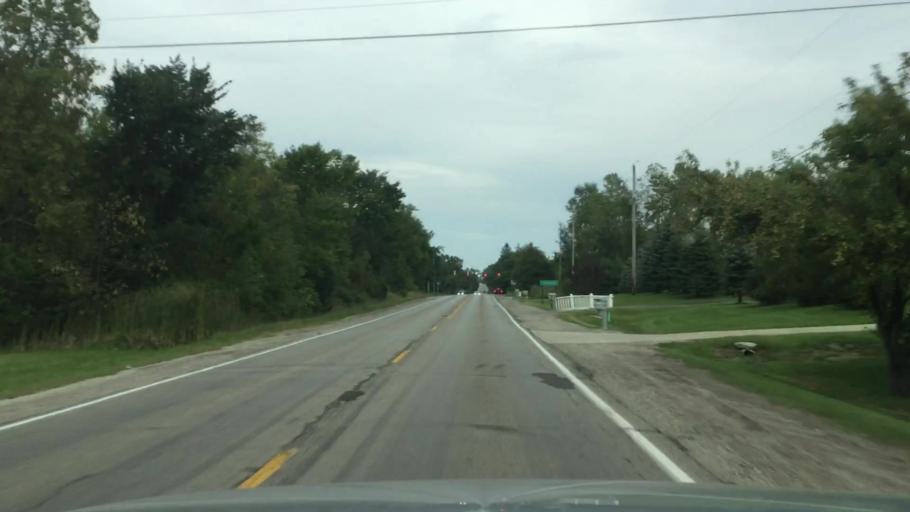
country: US
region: Michigan
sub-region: Genesee County
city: Lake Fenton
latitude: 42.8857
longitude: -83.7004
